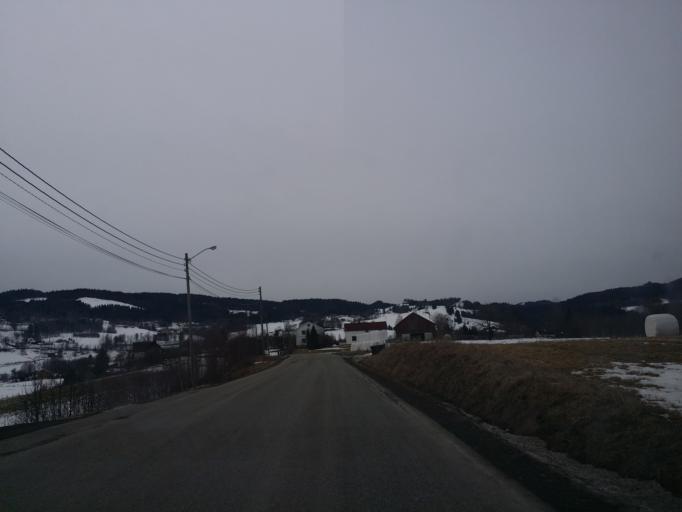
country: NO
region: Buskerud
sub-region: Lier
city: Tranby
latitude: 59.8568
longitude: 10.2361
